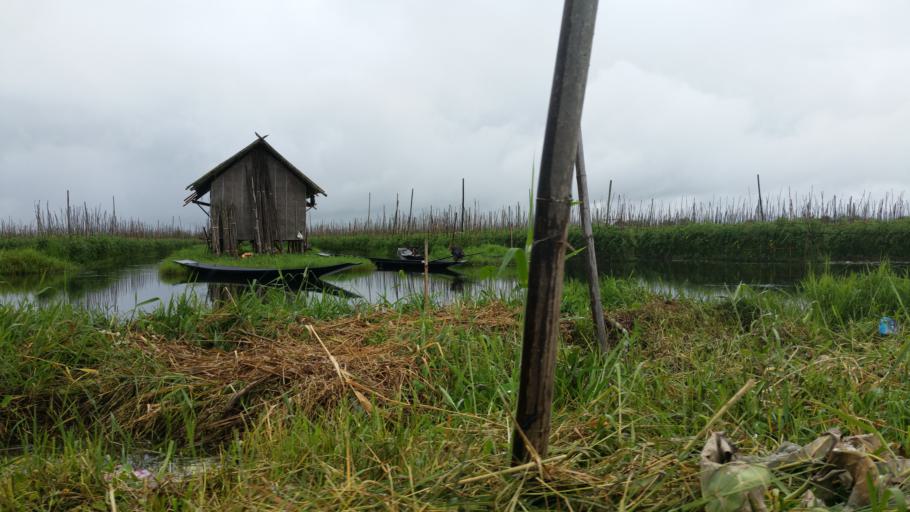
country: MM
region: Shan
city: Taunggyi
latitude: 20.5172
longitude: 96.8999
